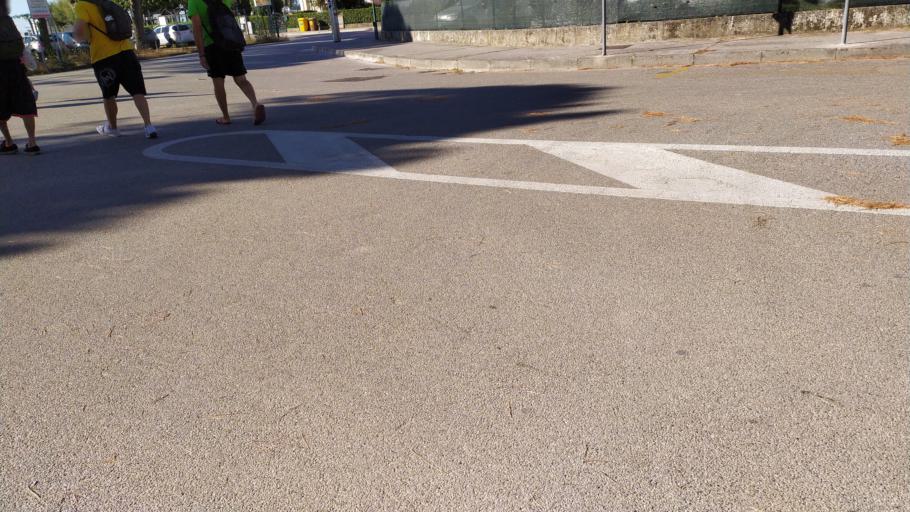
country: IT
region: Veneto
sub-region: Provincia di Venezia
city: Cavallino
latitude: 45.4786
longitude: 12.5735
